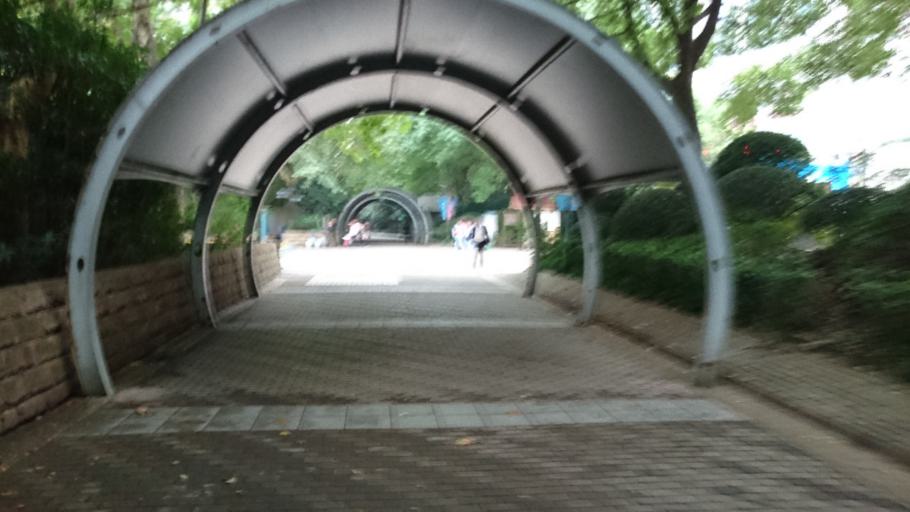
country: CN
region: Shanghai Shi
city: Shanghai
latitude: 31.2345
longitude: 121.4677
